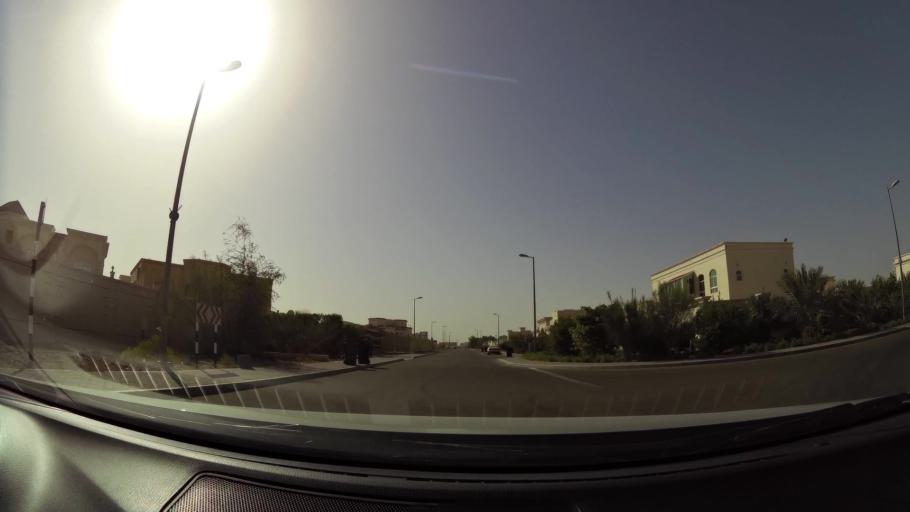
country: OM
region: Al Buraimi
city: Al Buraymi
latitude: 24.3563
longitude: 55.7913
